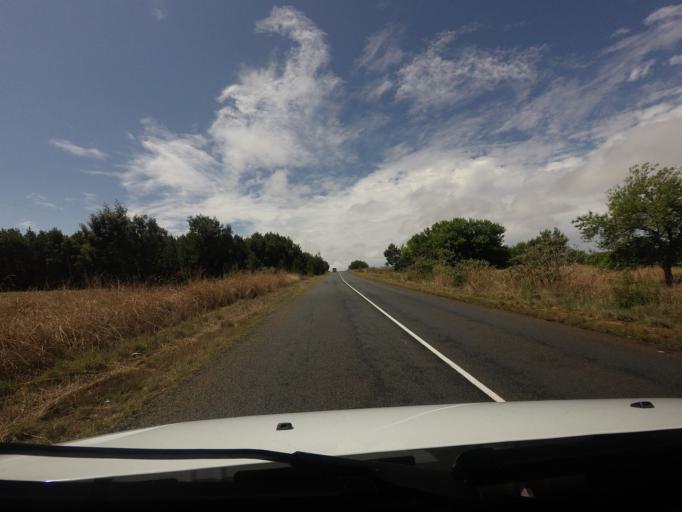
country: ZA
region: Mpumalanga
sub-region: Ehlanzeni District
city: Lydenburg
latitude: -25.1880
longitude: 30.3599
